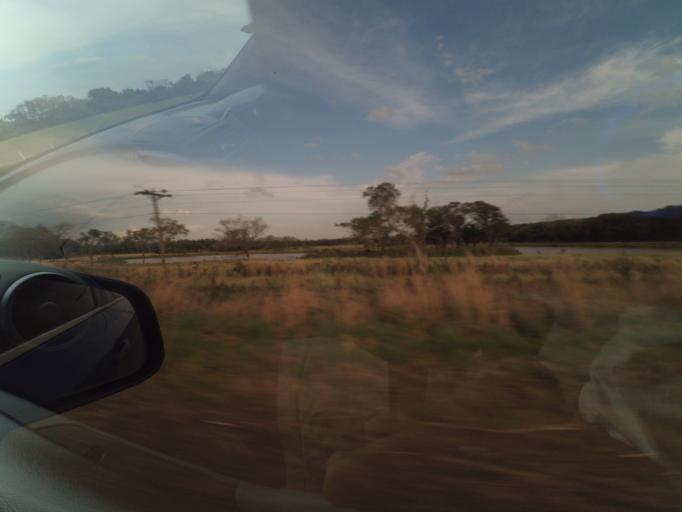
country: BO
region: Santa Cruz
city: Okinawa Numero Uno
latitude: -17.2330
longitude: -62.9461
